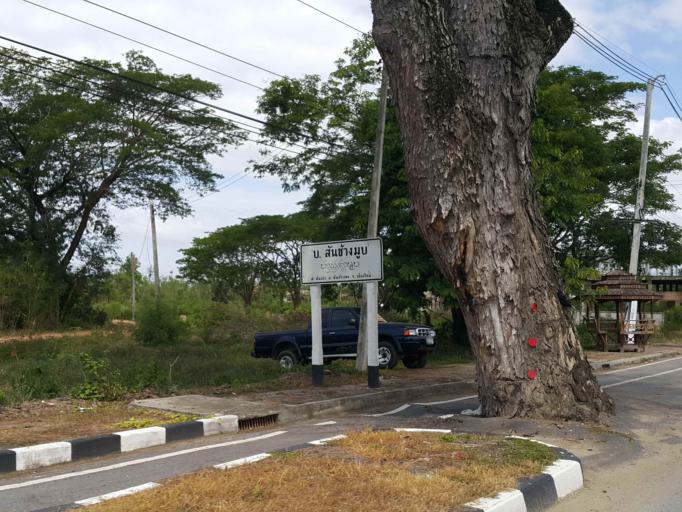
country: TH
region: Chiang Mai
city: San Kamphaeng
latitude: 18.7558
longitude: 99.0972
